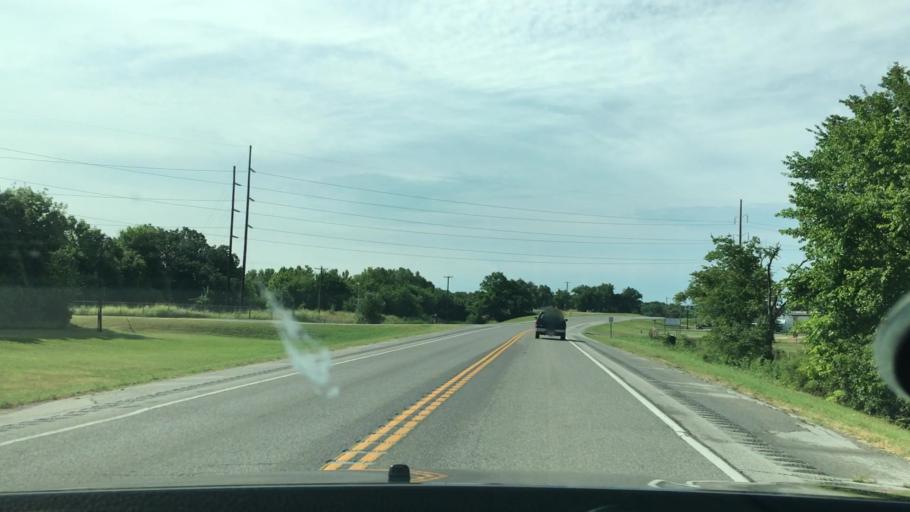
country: US
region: Oklahoma
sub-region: Murray County
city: Sulphur
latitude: 34.5238
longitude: -96.9696
